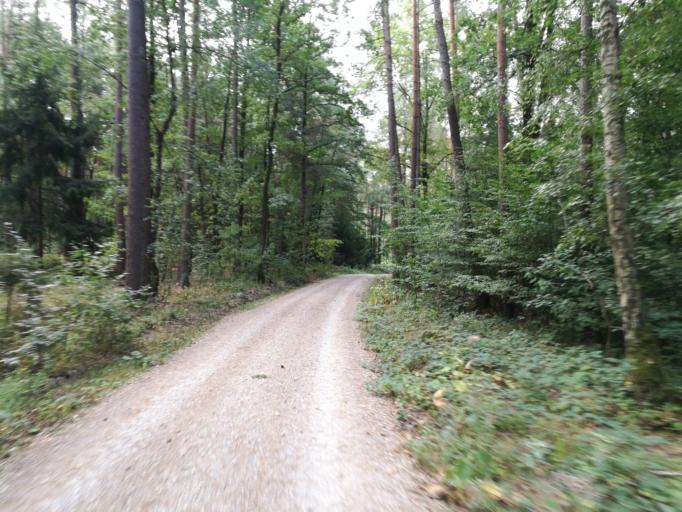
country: DE
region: Bavaria
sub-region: Regierungsbezirk Mittelfranken
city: Seukendorf
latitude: 49.4694
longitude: 10.9212
